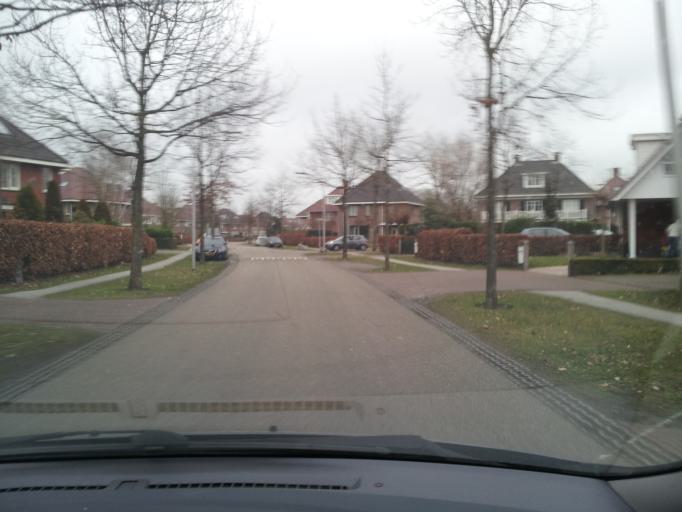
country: NL
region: South Holland
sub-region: Gemeente Den Haag
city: Ypenburg
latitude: 52.0459
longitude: 4.3627
